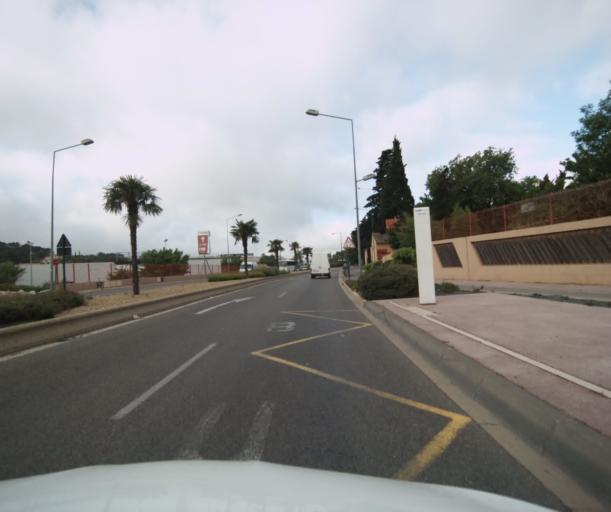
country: FR
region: Provence-Alpes-Cote d'Azur
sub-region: Departement du Var
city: Six-Fours-les-Plages
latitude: 43.1000
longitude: 5.8531
